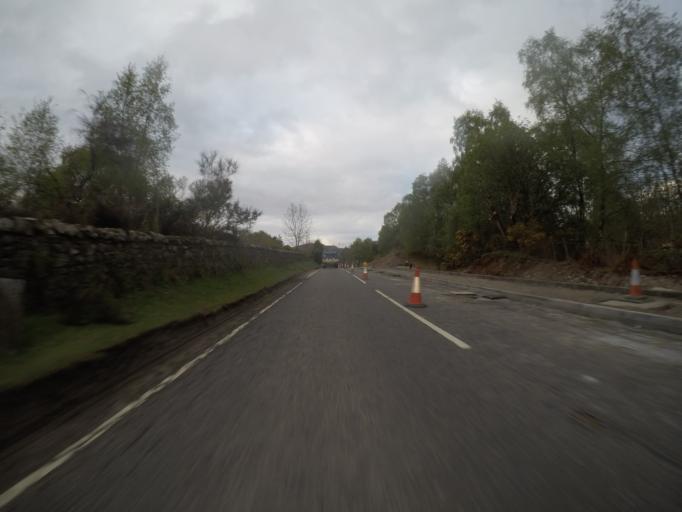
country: GB
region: Scotland
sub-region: Highland
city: Spean Bridge
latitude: 57.1357
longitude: -4.6888
